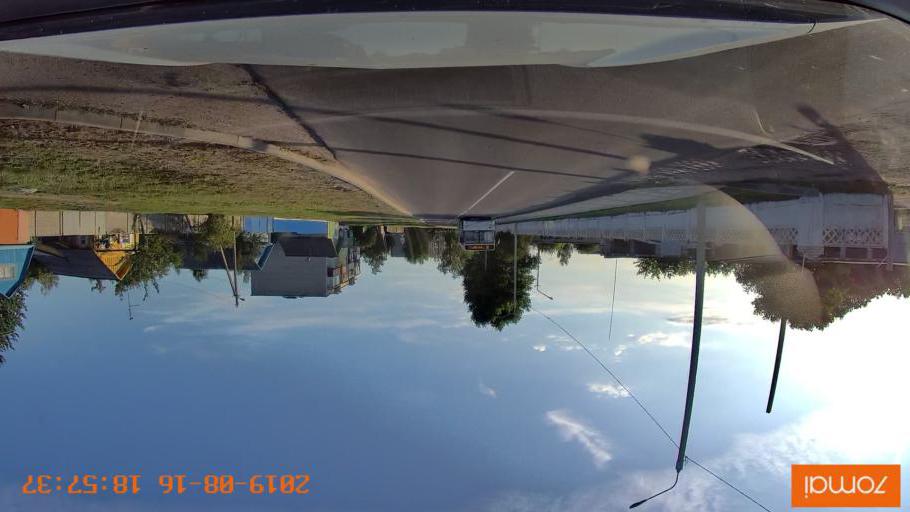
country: BY
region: Mogilev
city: Asipovichy
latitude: 53.2912
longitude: 28.6497
